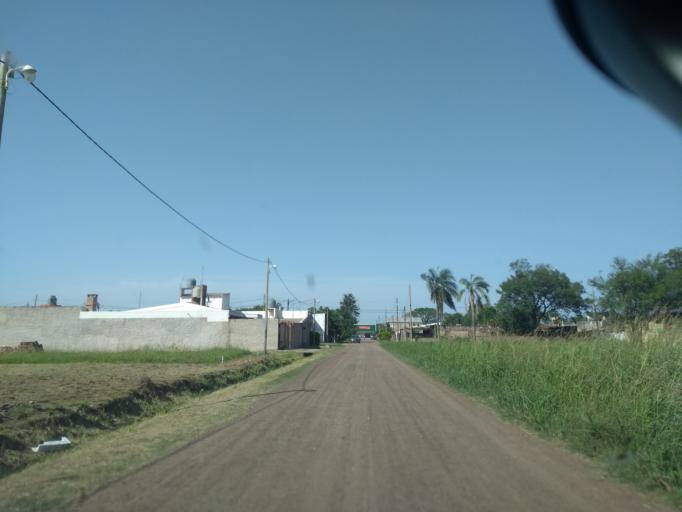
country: AR
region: Chaco
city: Fontana
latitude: -27.4156
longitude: -59.0370
